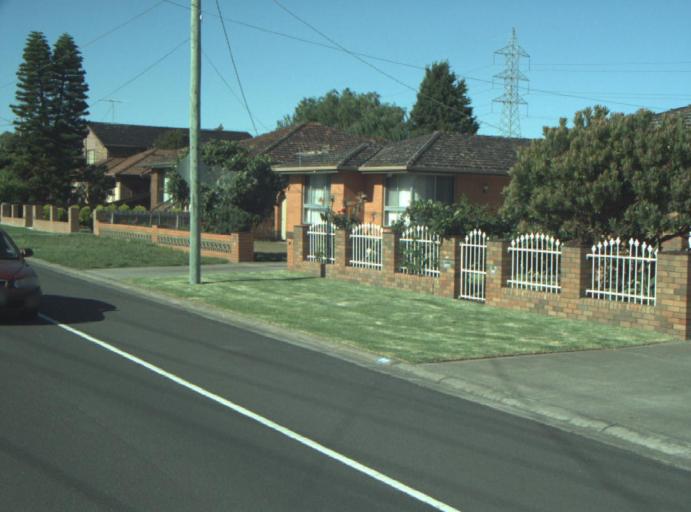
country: AU
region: Victoria
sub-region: Greater Geelong
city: Bell Post Hill
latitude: -38.0981
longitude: 144.3234
